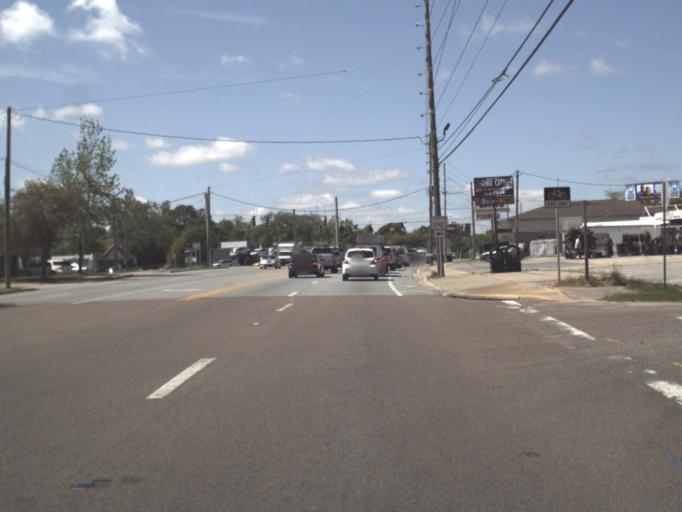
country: US
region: Florida
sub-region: Escambia County
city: Brent
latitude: 30.4577
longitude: -87.2383
